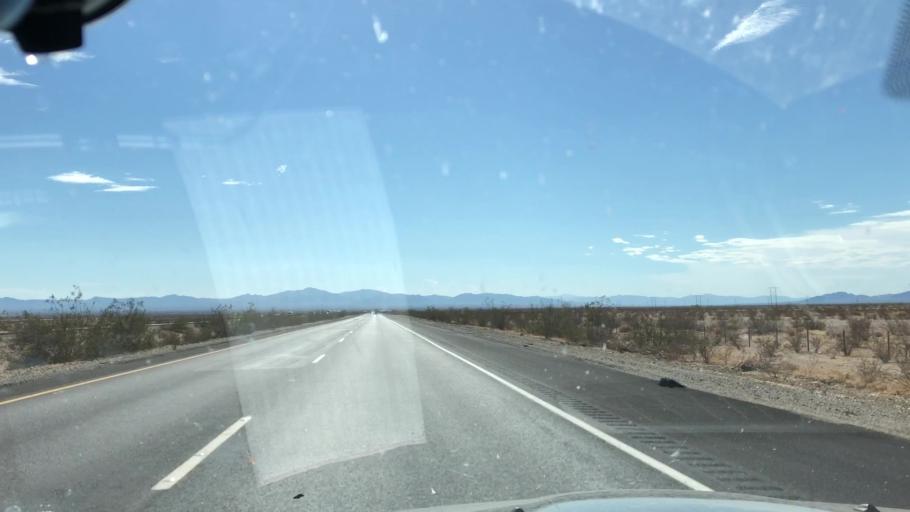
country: US
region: California
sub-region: Riverside County
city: Mesa Verde
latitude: 33.6097
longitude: -114.8521
